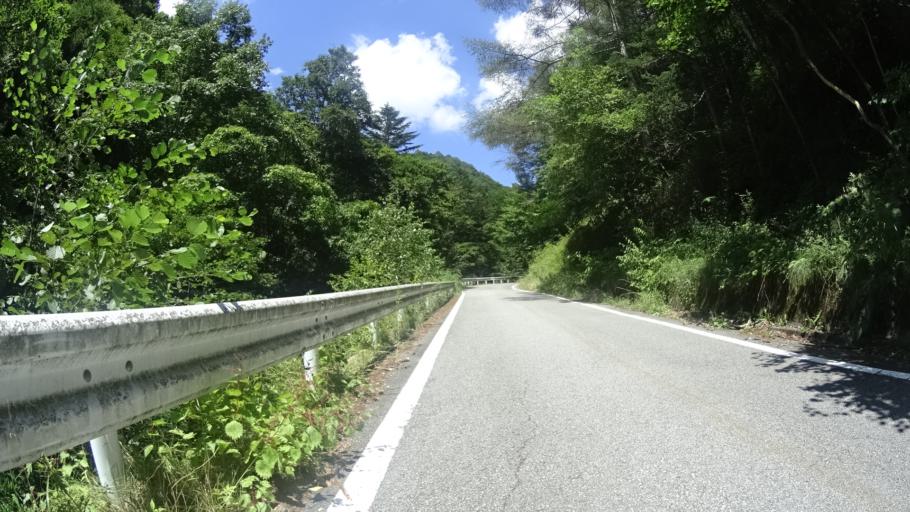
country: JP
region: Yamanashi
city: Enzan
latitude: 35.8179
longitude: 138.6542
